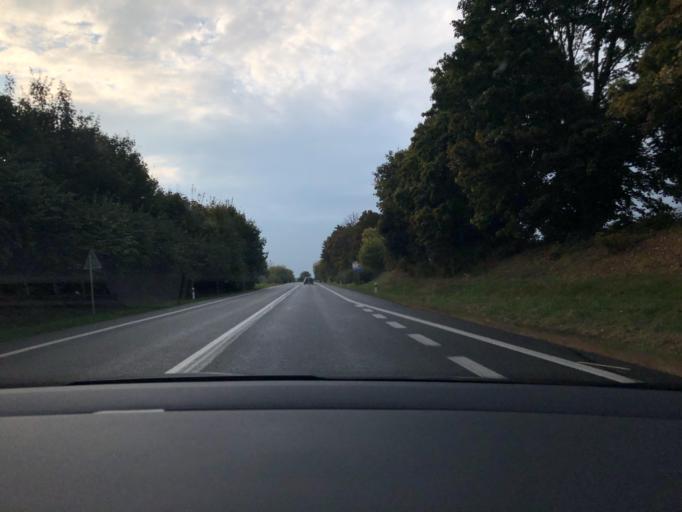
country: CZ
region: Central Bohemia
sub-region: Okres Kolin
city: Kolin
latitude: 50.0334
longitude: 15.1636
